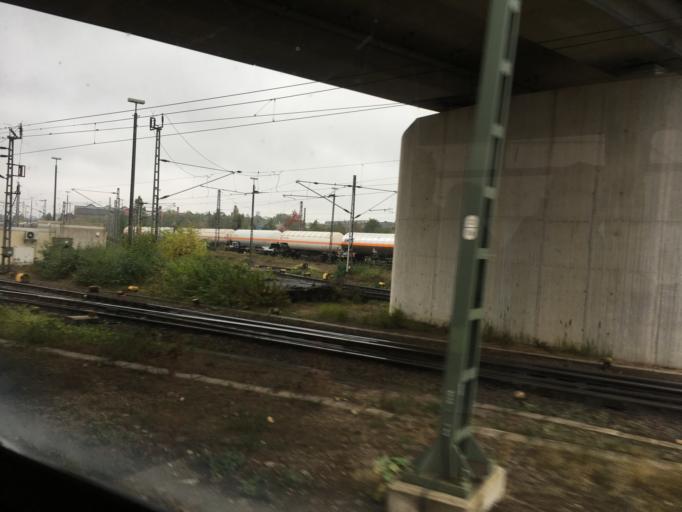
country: DE
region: Lower Saxony
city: Osnabrueck
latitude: 52.2681
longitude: 8.0843
